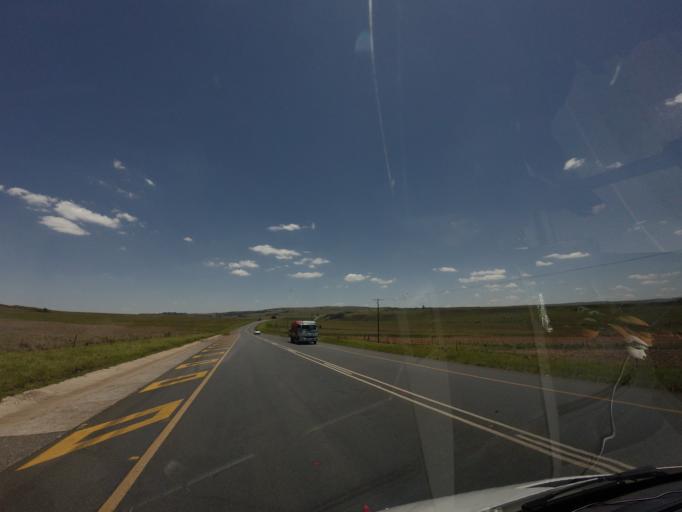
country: ZA
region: Mpumalanga
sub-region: Nkangala District Municipality
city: Belfast
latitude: -25.7061
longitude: 30.1875
